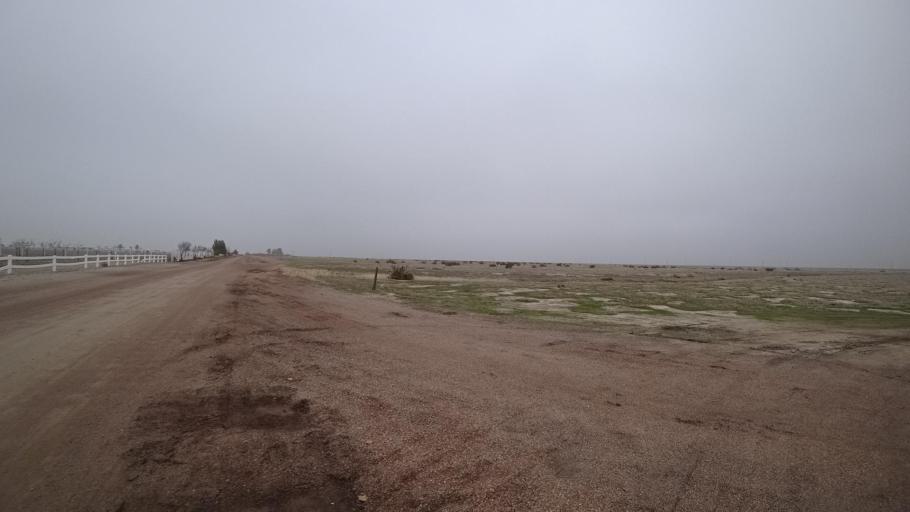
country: US
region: California
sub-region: Tulare County
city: Alpaugh
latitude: 35.7259
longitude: -119.4726
